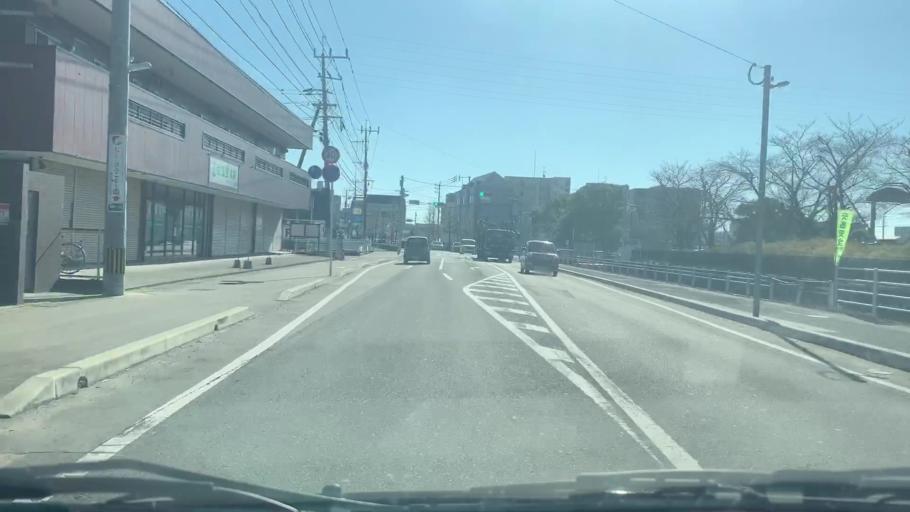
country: JP
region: Saga Prefecture
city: Saga-shi
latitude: 33.2840
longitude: 130.2686
